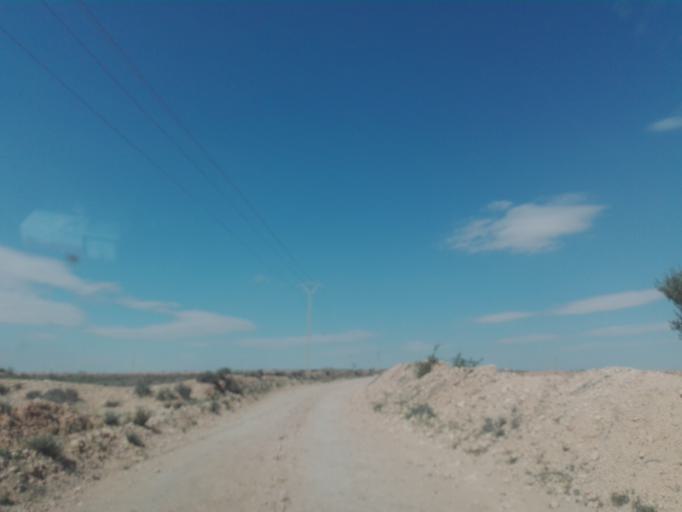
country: TN
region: Safaqis
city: Sfax
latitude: 34.6870
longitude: 10.5482
